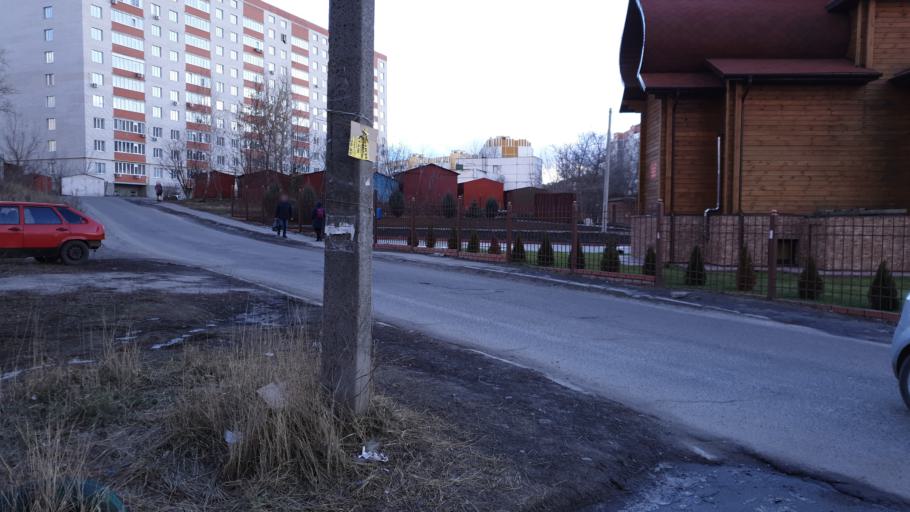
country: RU
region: Kursk
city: Kursk
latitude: 51.7271
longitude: 36.1479
